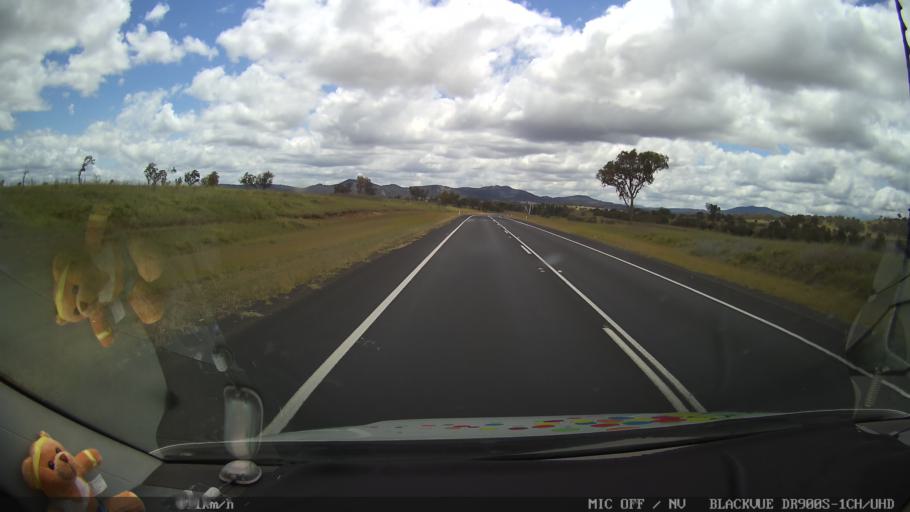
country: AU
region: New South Wales
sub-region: Glen Innes Severn
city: Glen Innes
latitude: -29.3941
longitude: 151.8802
